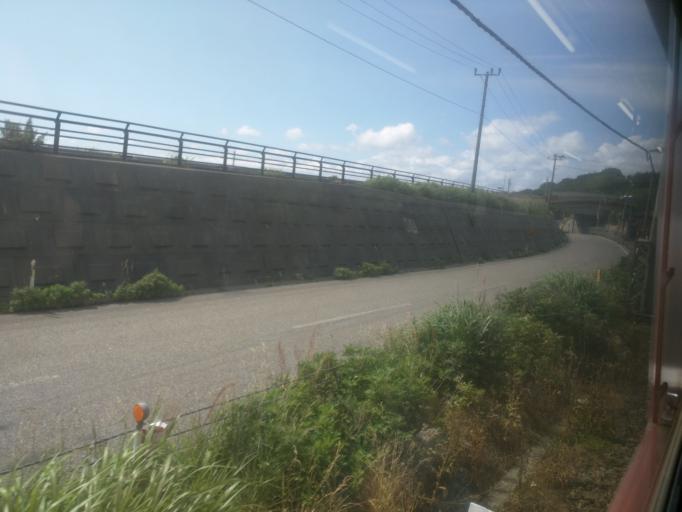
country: JP
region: Yamagata
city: Tsuruoka
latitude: 38.5494
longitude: 139.5507
